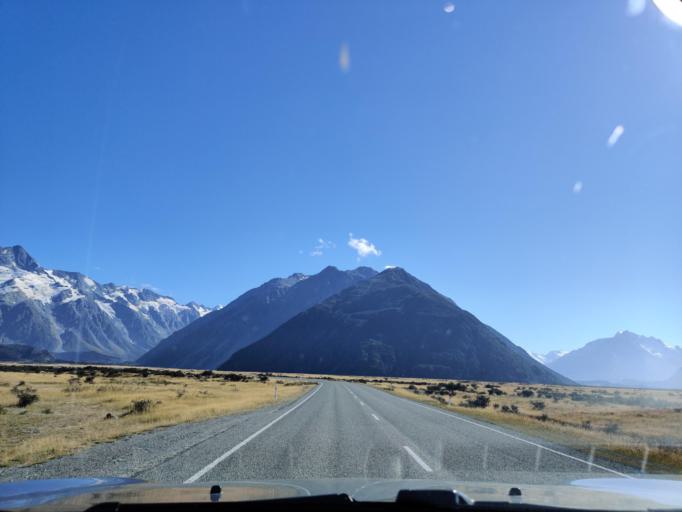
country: NZ
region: Canterbury
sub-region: Timaru District
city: Pleasant Point
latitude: -43.7542
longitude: 170.1179
